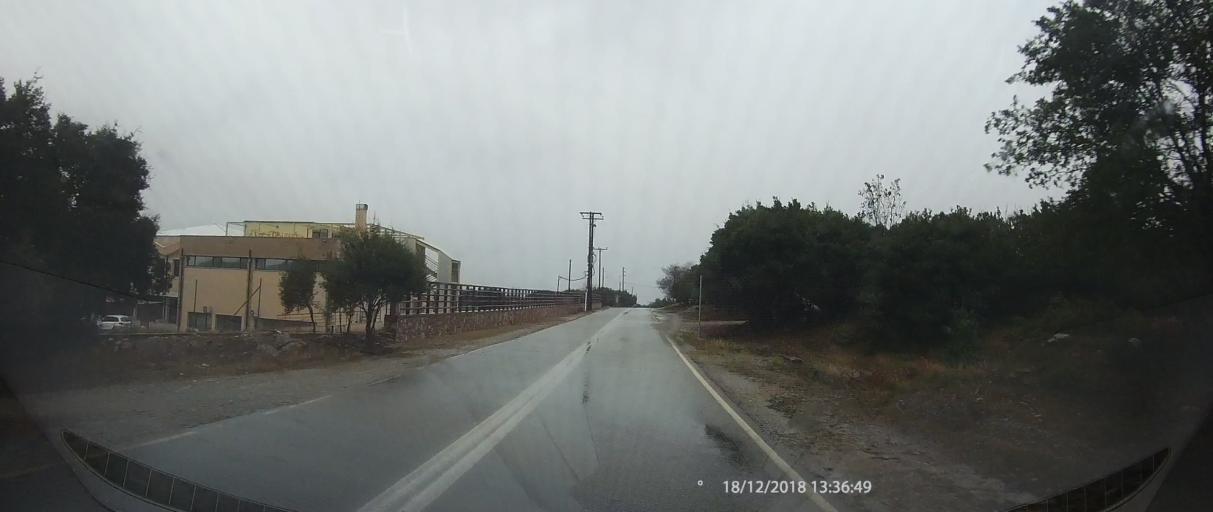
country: GR
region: Central Macedonia
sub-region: Nomos Pierias
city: Litochoro
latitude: 40.1101
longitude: 22.4980
